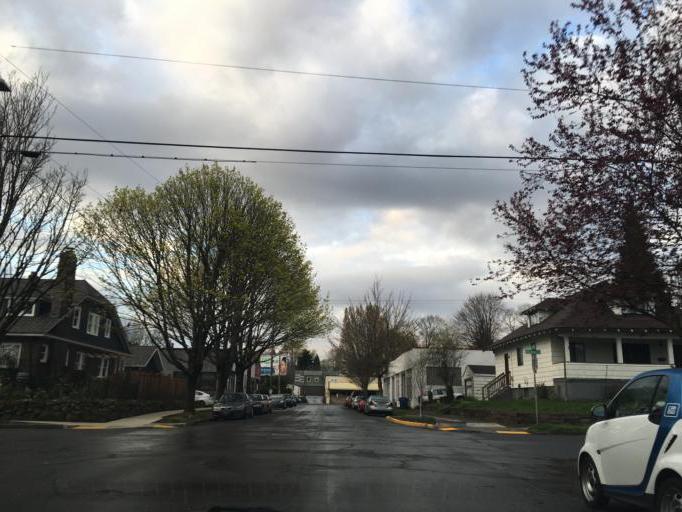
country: US
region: Oregon
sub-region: Multnomah County
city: Portland
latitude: 45.5039
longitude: -122.6404
